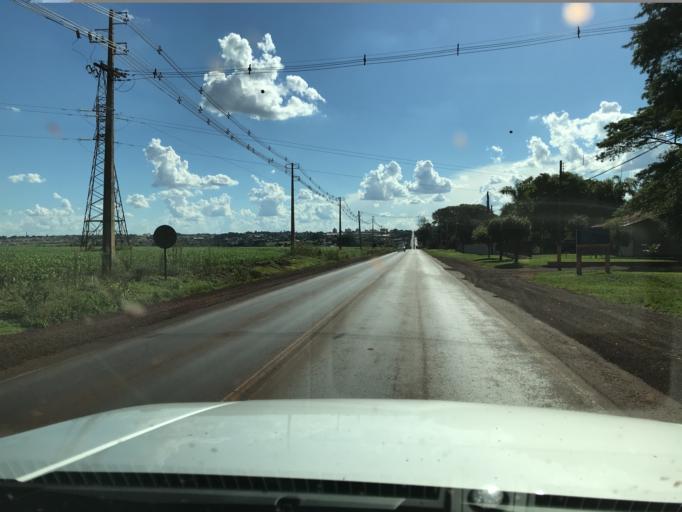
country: BR
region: Parana
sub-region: Palotina
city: Palotina
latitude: -24.2757
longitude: -53.8123
